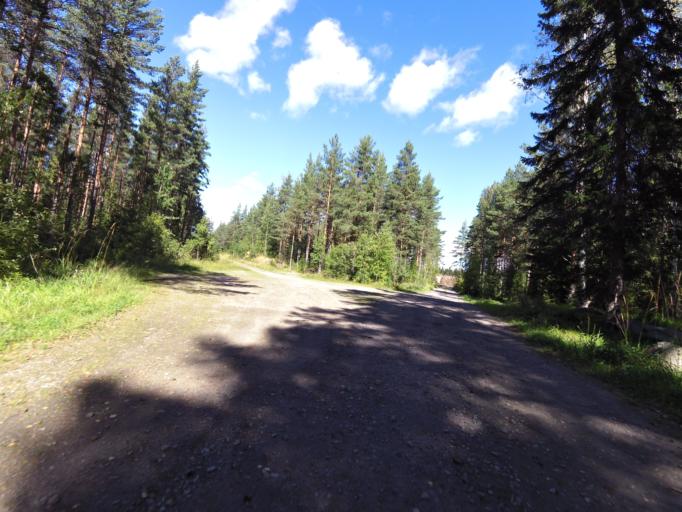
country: SE
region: Gaevleborg
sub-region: Gavle Kommun
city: Valbo
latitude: 60.7263
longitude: 17.0005
